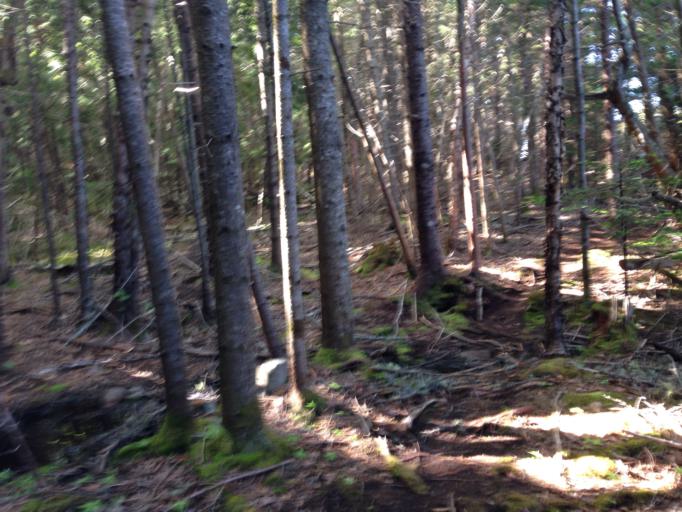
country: US
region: Maine
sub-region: Hancock County
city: Gouldsboro
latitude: 44.3873
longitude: -68.0736
